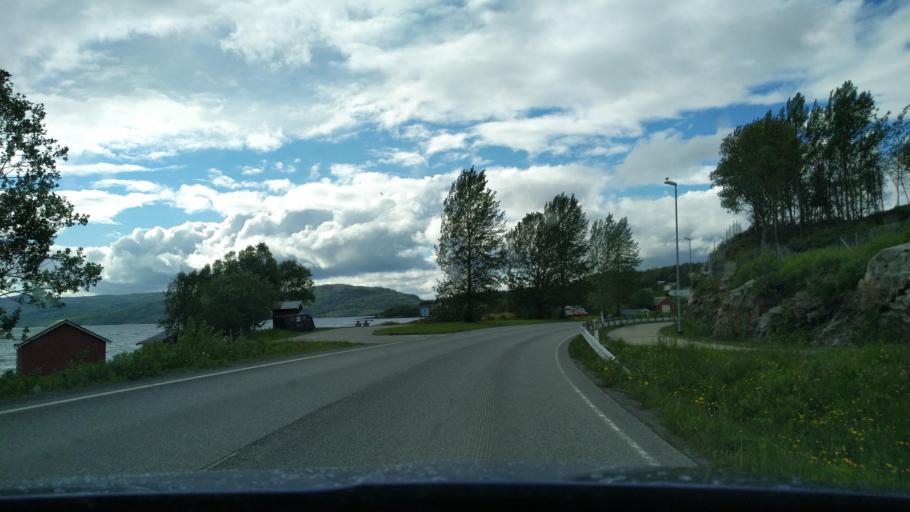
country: NO
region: Troms
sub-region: Sorreisa
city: Sorreisa
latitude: 69.1742
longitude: 18.0851
